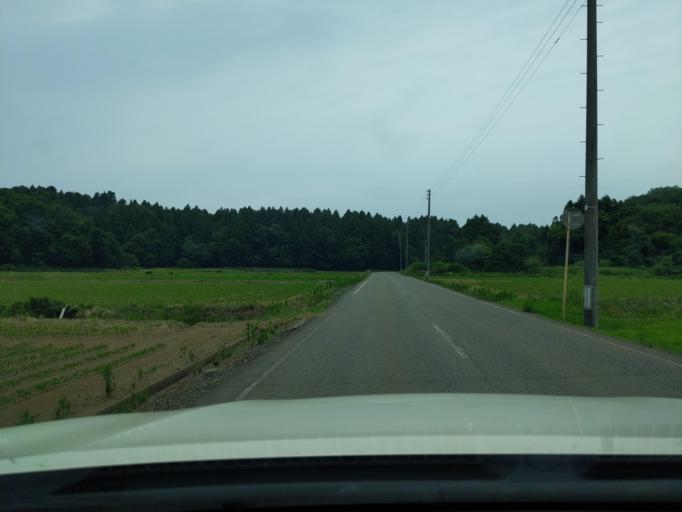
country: JP
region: Niigata
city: Kashiwazaki
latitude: 37.3331
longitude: 138.5565
